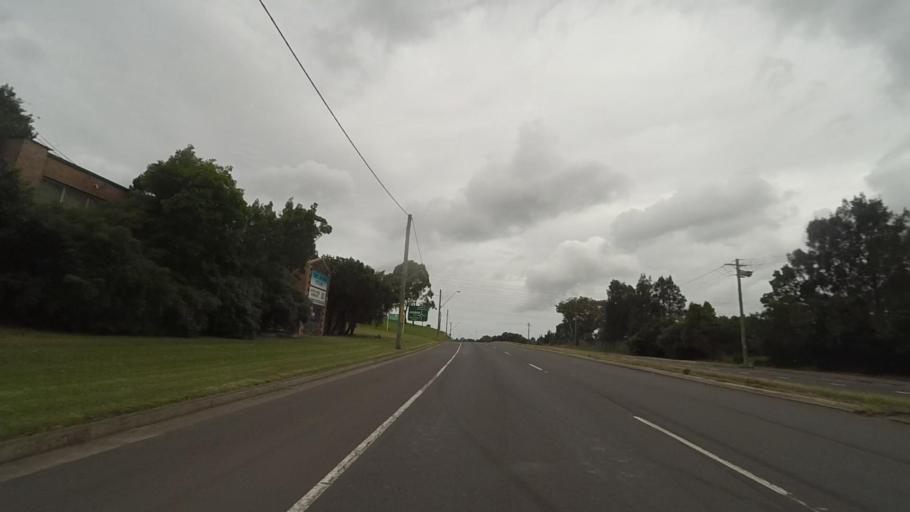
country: AU
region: New South Wales
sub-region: Wollongong
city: Berkeley
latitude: -34.4716
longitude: 150.8291
